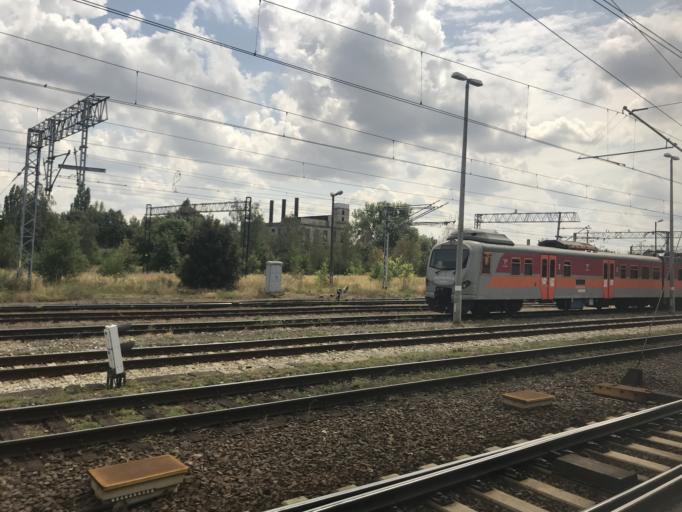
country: PL
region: Greater Poland Voivodeship
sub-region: Poznan
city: Poznan
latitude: 52.3975
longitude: 16.9103
